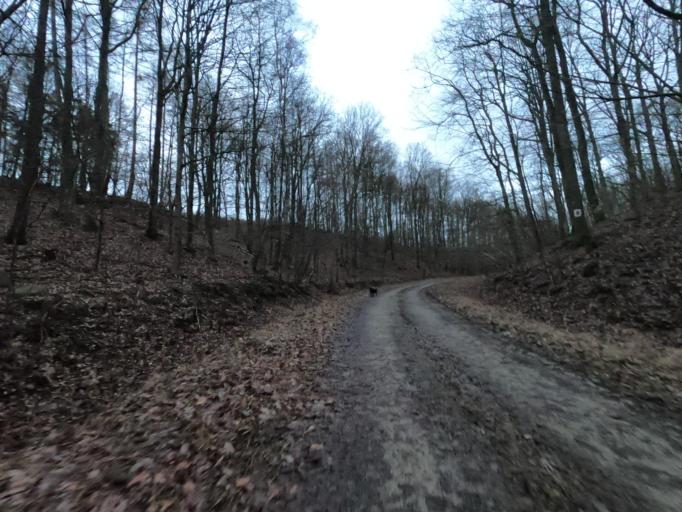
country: PL
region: Greater Poland Voivodeship
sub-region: Powiat pilski
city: Wyrzysk
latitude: 53.1223
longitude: 17.2197
